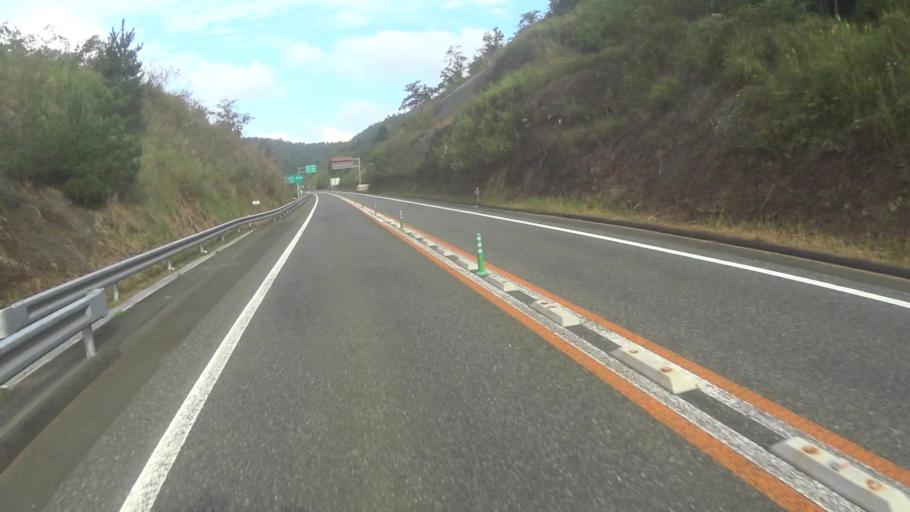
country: JP
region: Kyoto
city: Ayabe
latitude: 35.3395
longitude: 135.3059
